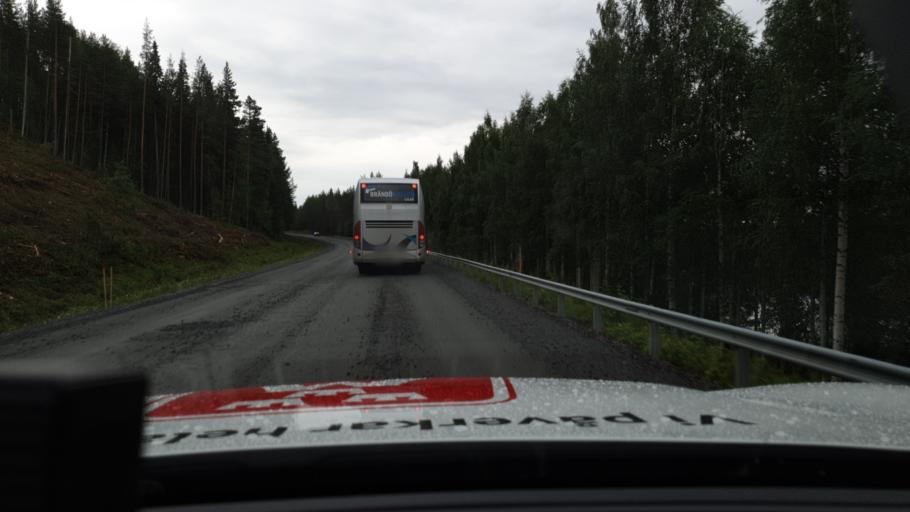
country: SE
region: Norrbotten
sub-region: Alvsbyns Kommun
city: AElvsbyn
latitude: 66.1457
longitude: 20.8760
